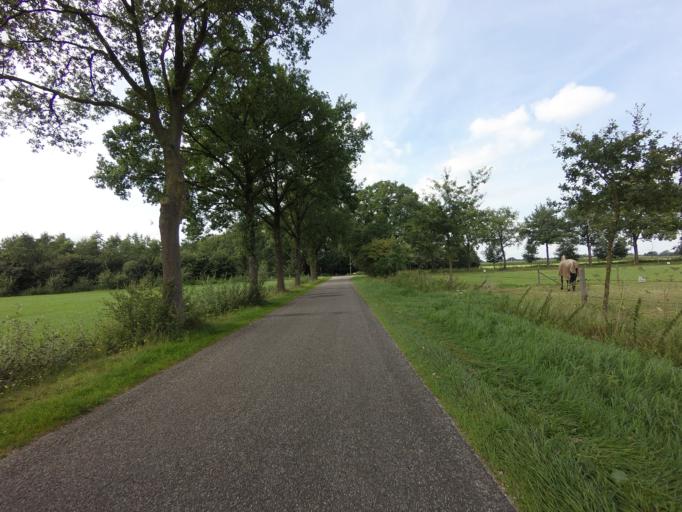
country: DE
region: Lower Saxony
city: Lage
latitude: 52.4297
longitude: 6.9346
